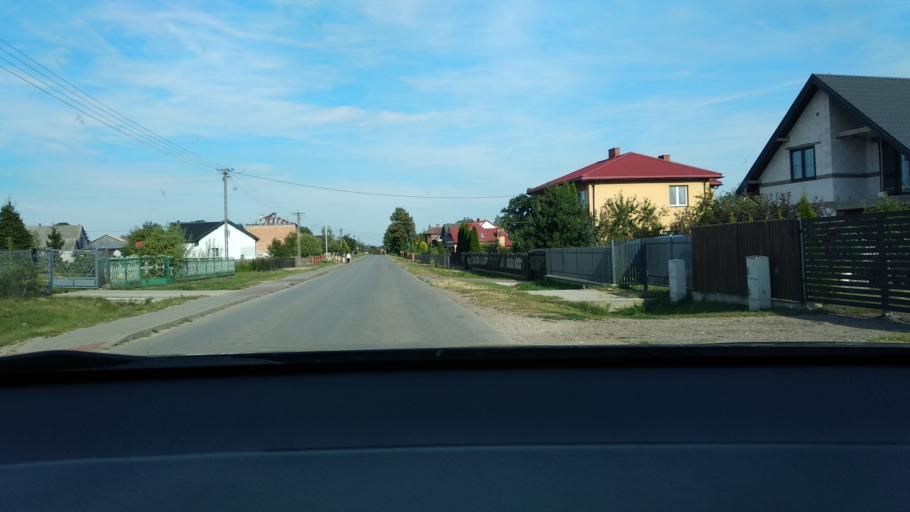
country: PL
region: Masovian Voivodeship
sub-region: Powiat pultuski
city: Obryte
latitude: 52.7140
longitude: 21.1855
